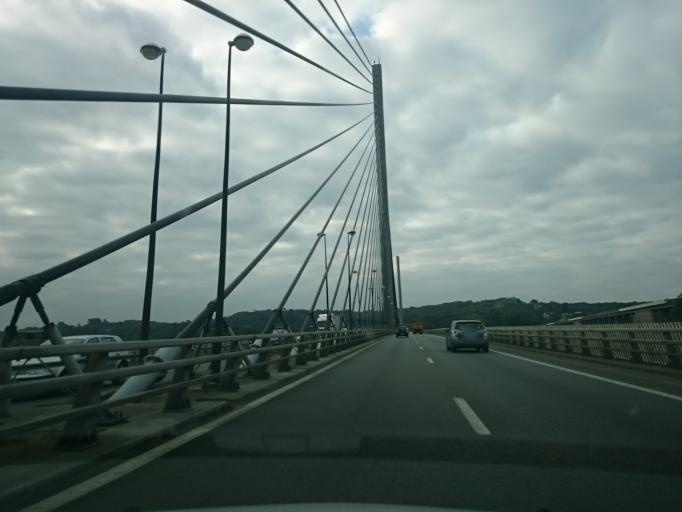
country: FR
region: Brittany
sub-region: Departement du Finistere
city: Le Relecq-Kerhuon
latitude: 48.3909
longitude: -4.4017
